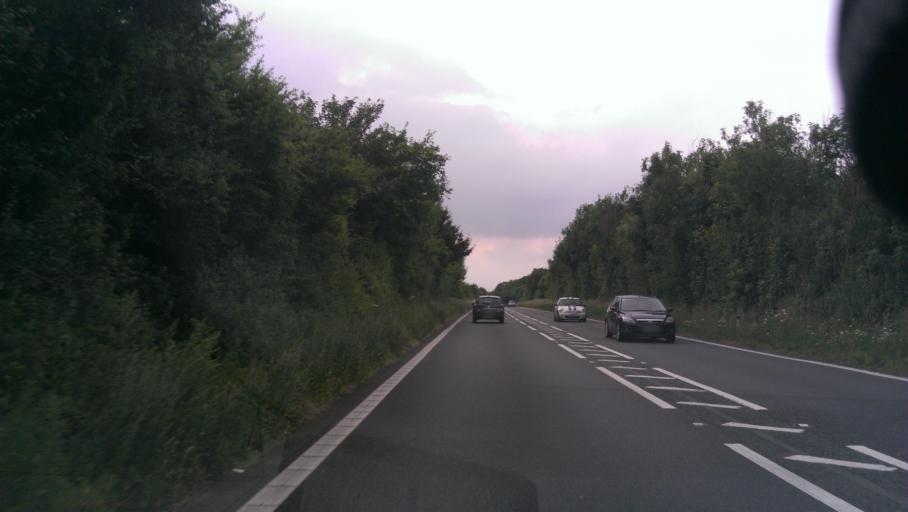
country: GB
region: England
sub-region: Kent
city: Shepherdswell
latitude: 51.1673
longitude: 1.2551
